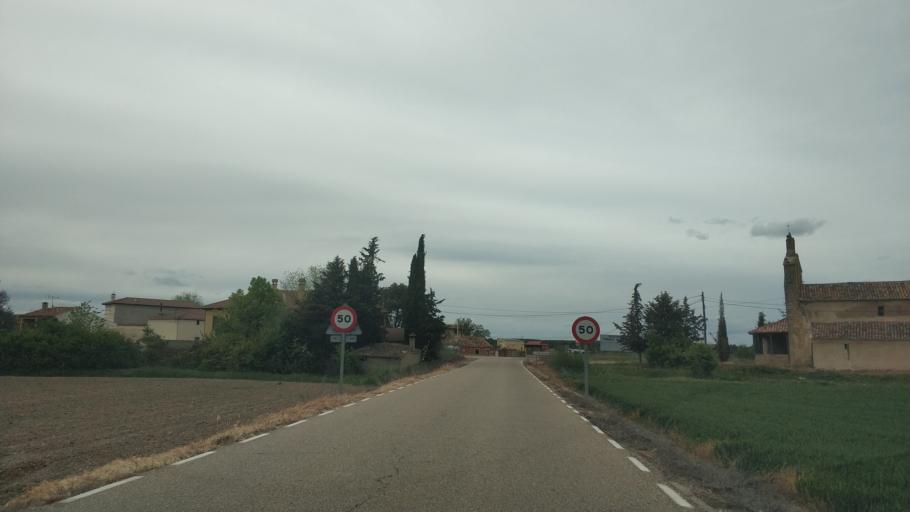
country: ES
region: Castille and Leon
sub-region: Provincia de Soria
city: Berlanga de Duero
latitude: 41.4939
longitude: -2.8686
